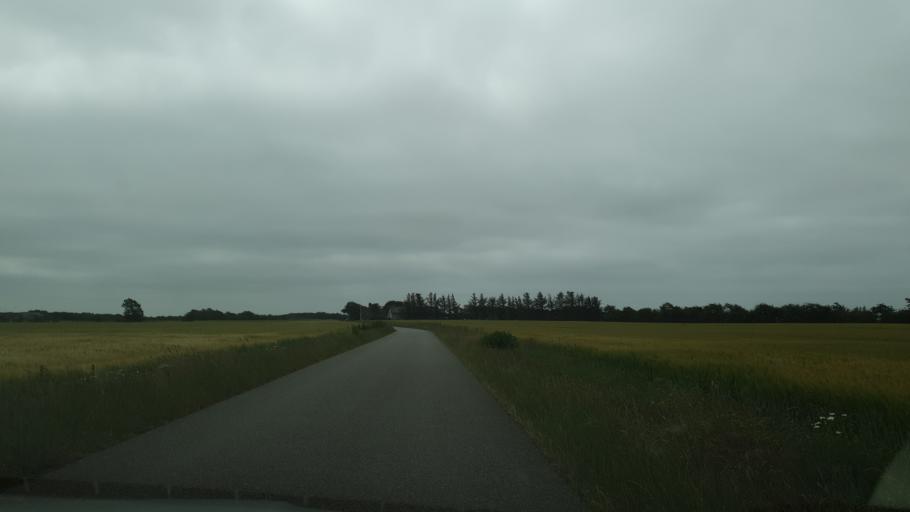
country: DK
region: Central Jutland
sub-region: Ringkobing-Skjern Kommune
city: Skjern
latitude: 55.9492
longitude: 8.4053
